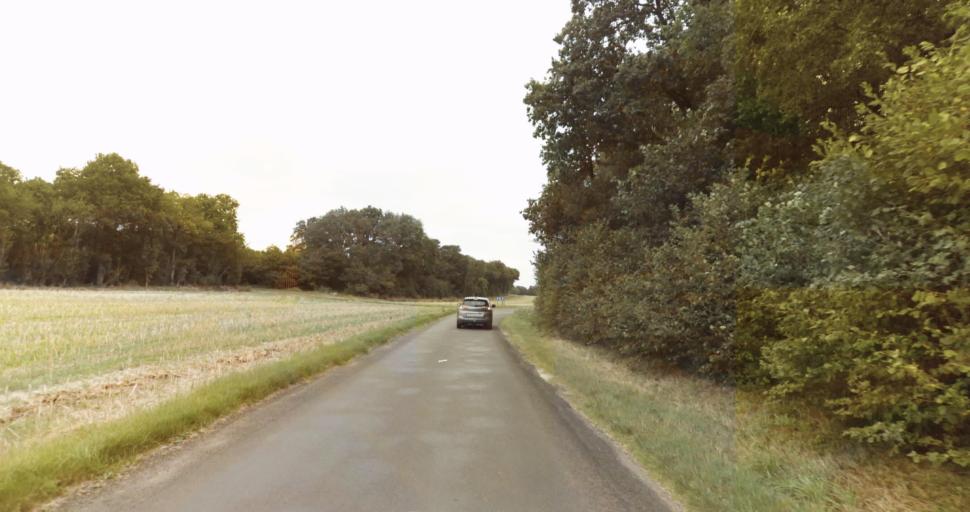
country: FR
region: Haute-Normandie
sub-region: Departement de l'Eure
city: Evreux
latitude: 48.9609
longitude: 1.2462
